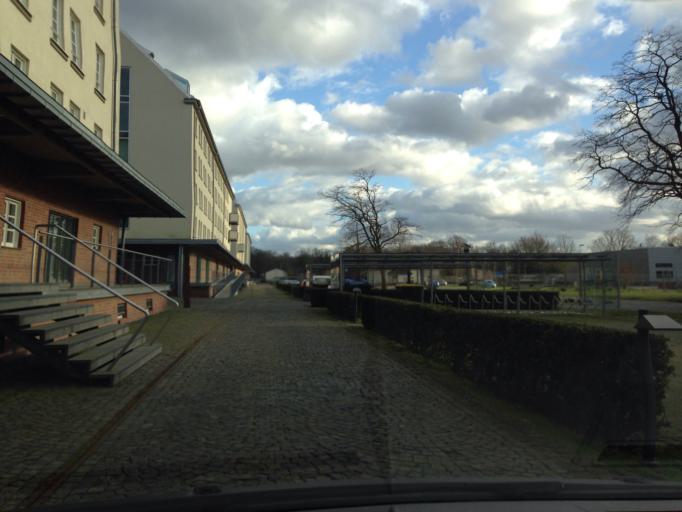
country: DE
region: North Rhine-Westphalia
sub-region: Regierungsbezirk Munster
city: Muenster
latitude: 51.9993
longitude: 7.6344
